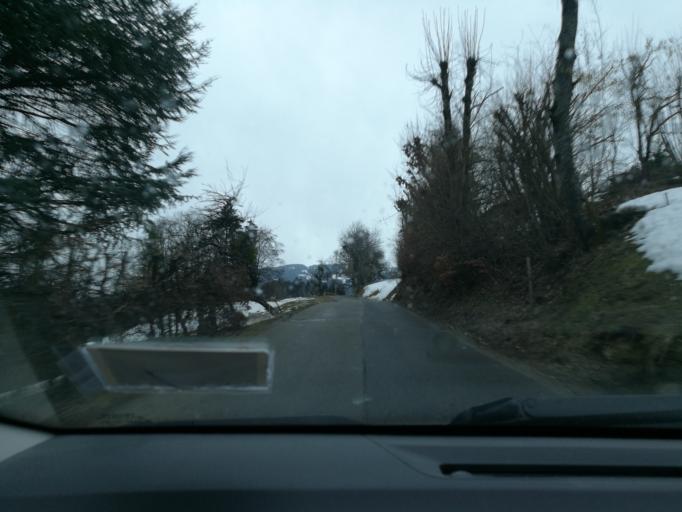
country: FR
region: Rhone-Alpes
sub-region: Departement de la Haute-Savoie
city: Combloux
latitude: 45.9108
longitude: 6.6318
